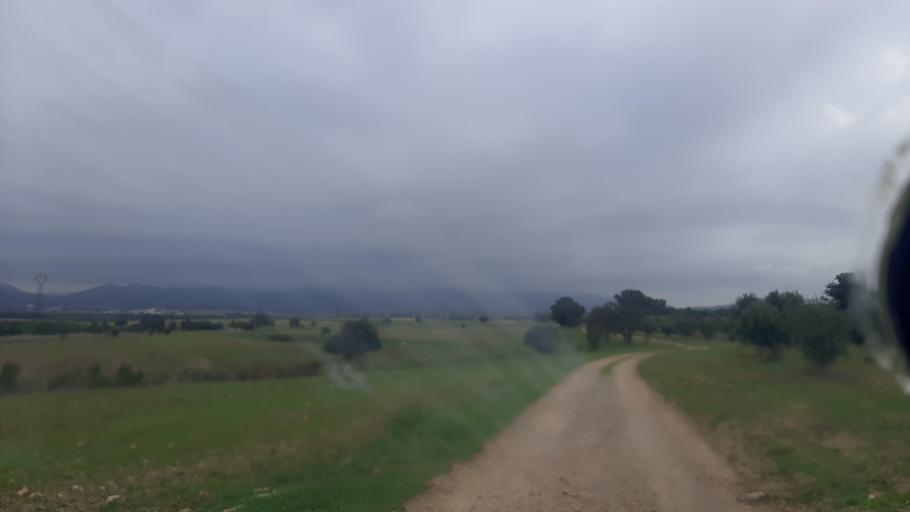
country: TN
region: Tunis
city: La Sebala du Mornag
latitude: 36.5735
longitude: 10.2937
